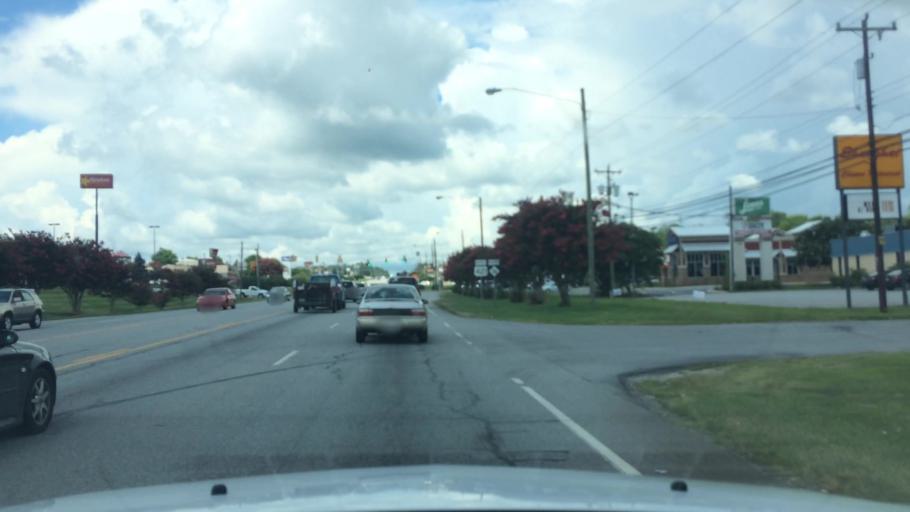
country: US
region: North Carolina
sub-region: Wilkes County
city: Cricket
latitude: 36.1504
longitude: -81.1935
